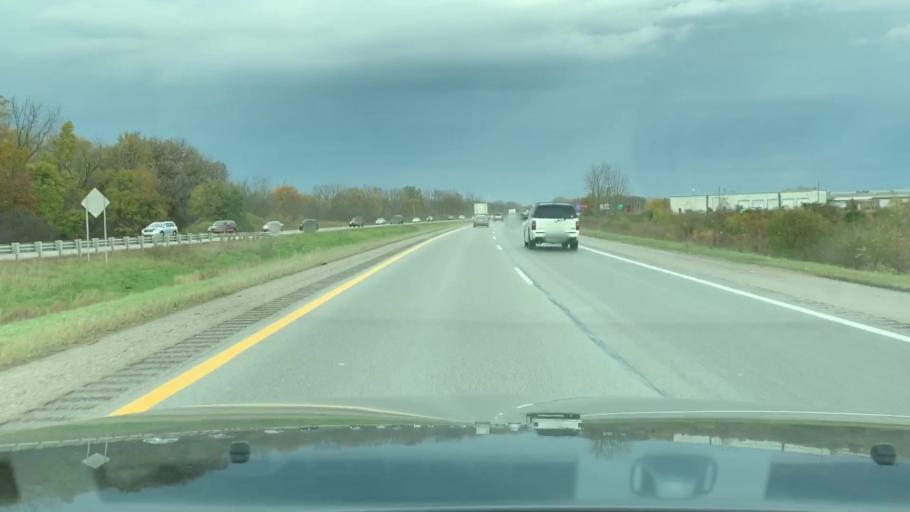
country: US
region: Michigan
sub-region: Kent County
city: Grandville
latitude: 42.9205
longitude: -85.7583
